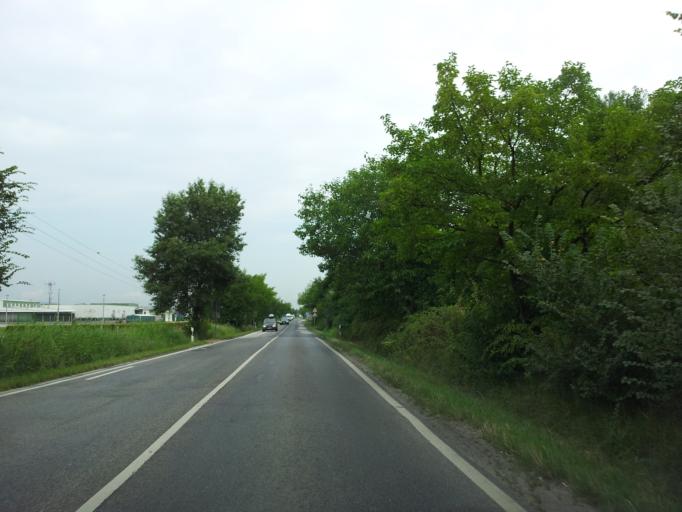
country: HU
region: Pest
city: Szigetszentmiklos
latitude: 47.3720
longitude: 19.0486
